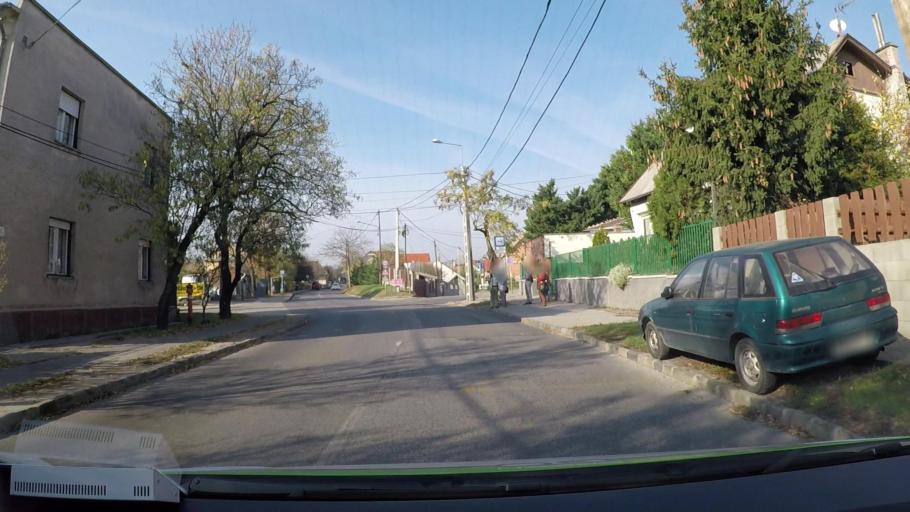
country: HU
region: Budapest
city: Budapest XXII. keruelet
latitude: 47.4228
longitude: 19.0306
